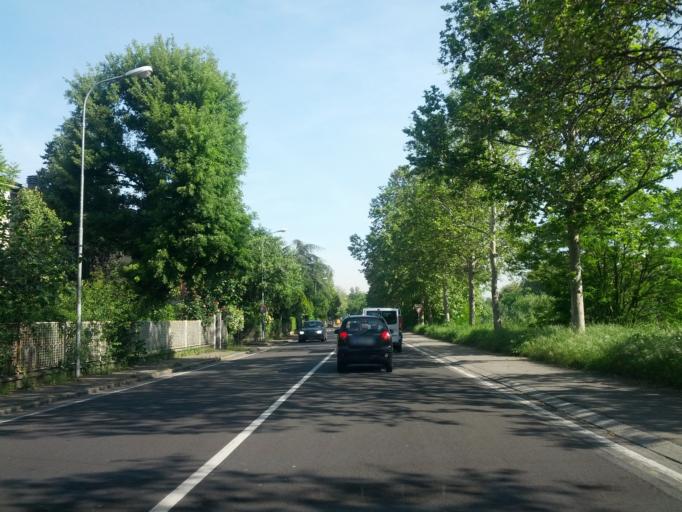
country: IT
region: Emilia-Romagna
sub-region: Provincia di Reggio Emilia
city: Reggio nell'Emilia
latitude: 44.7075
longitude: 10.6201
